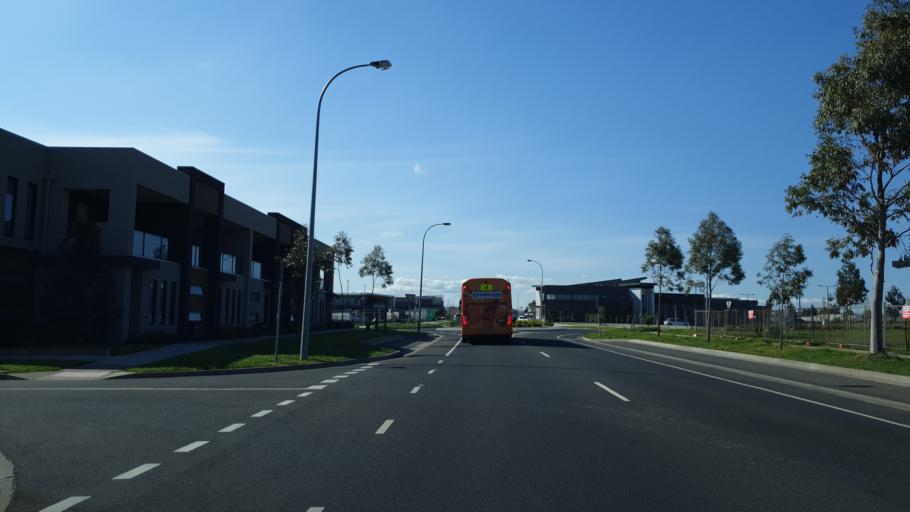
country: AU
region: Victoria
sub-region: Casey
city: Cranbourne East
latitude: -38.1059
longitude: 145.3250
